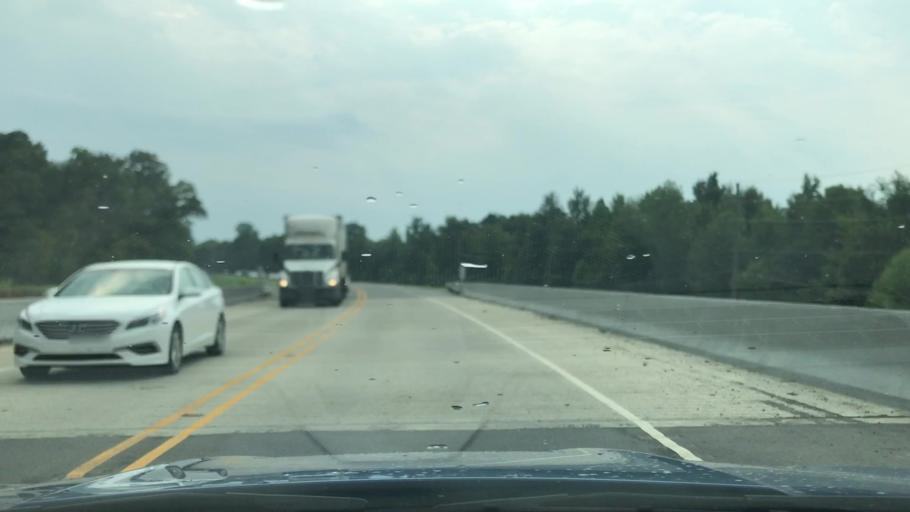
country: US
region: Louisiana
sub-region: Caddo Parish
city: Greenwood
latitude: 32.4569
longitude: -94.0151
